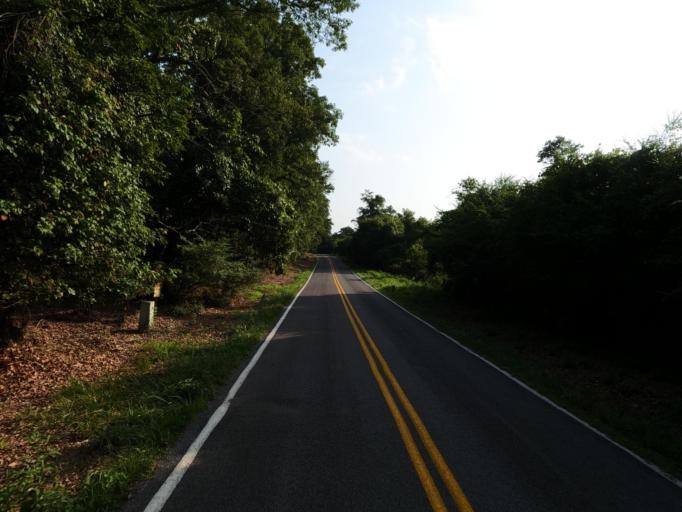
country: US
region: West Virginia
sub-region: Morgan County
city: Berkeley Springs
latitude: 39.6399
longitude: -78.2998
